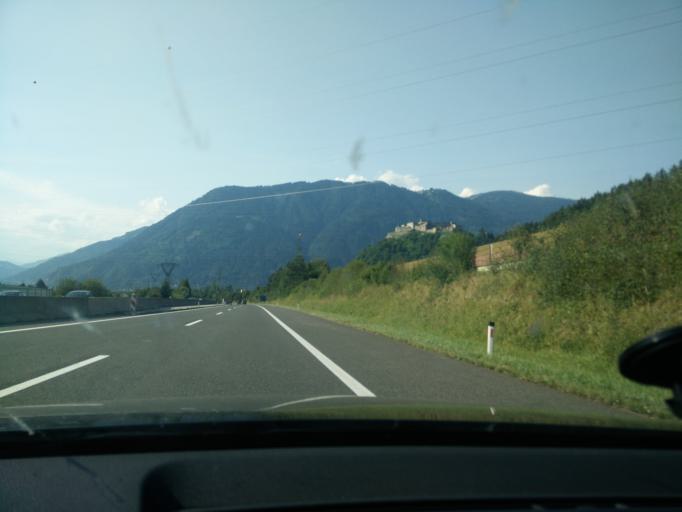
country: AT
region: Carinthia
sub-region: Politischer Bezirk Villach Land
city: Wernberg
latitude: 46.6311
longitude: 13.8959
